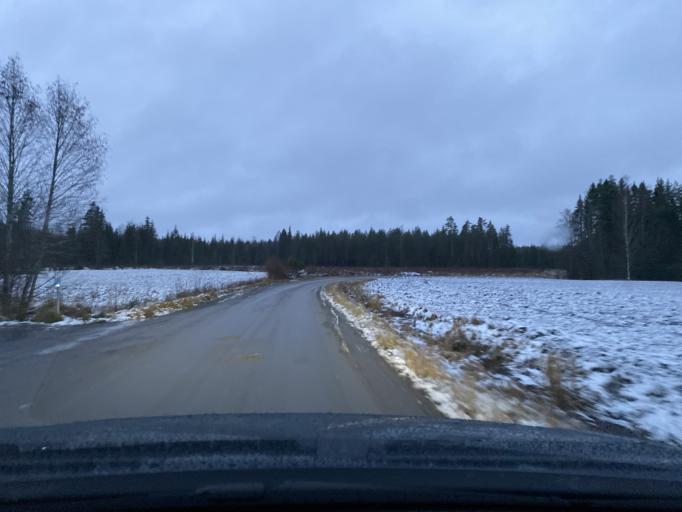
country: FI
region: Pirkanmaa
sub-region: Lounais-Pirkanmaa
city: Punkalaidun
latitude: 61.1449
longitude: 22.9509
